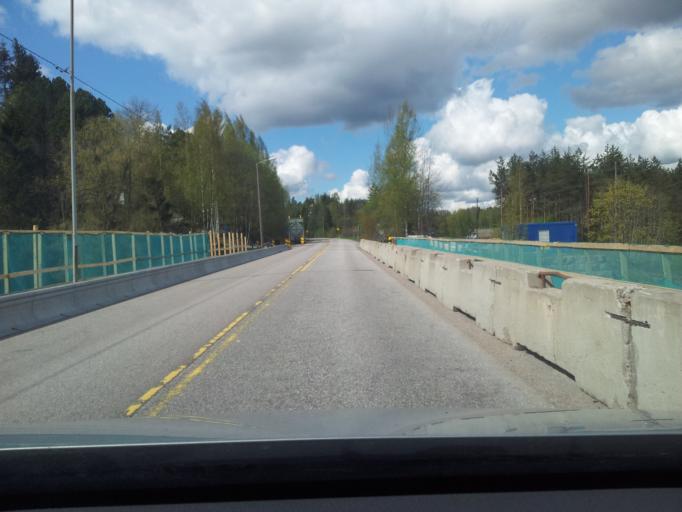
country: FI
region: Uusimaa
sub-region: Loviisa
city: Perna
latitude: 60.5032
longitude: 25.9430
